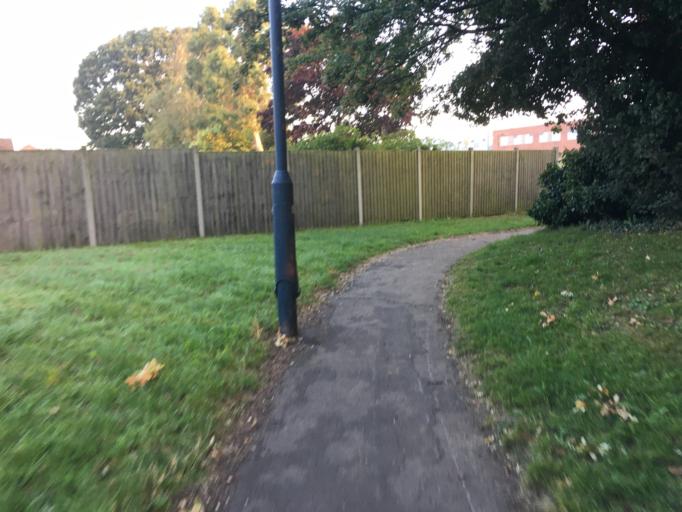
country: GB
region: England
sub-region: Warwickshire
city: Rugby
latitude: 52.3549
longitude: -1.2635
